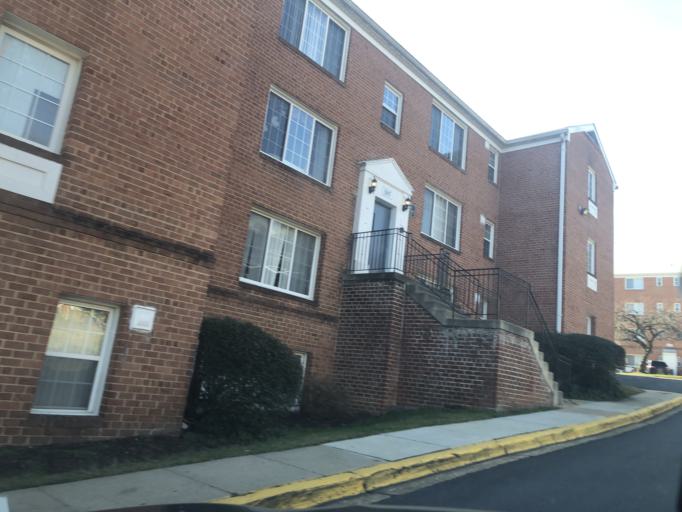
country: US
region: Maryland
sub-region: Montgomery County
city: Silver Spring
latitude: 38.9973
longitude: -77.0420
